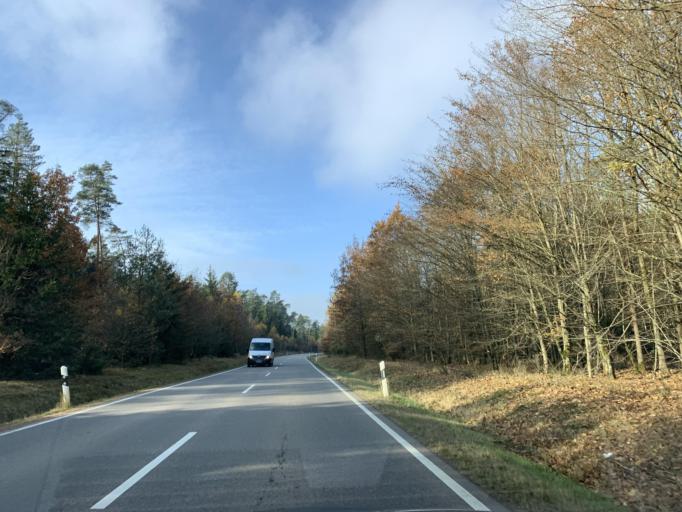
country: DE
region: Bavaria
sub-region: Upper Palatinate
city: Nittenau
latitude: 49.2463
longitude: 12.2468
